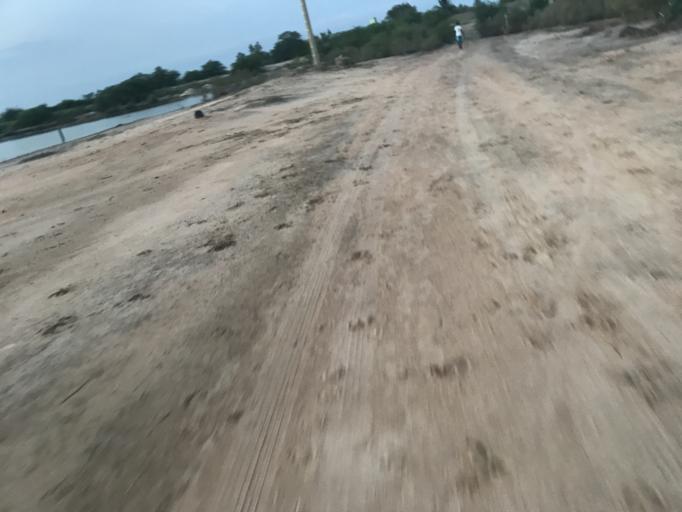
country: SN
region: Saint-Louis
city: Saint-Louis
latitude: 16.0570
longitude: -16.4080
